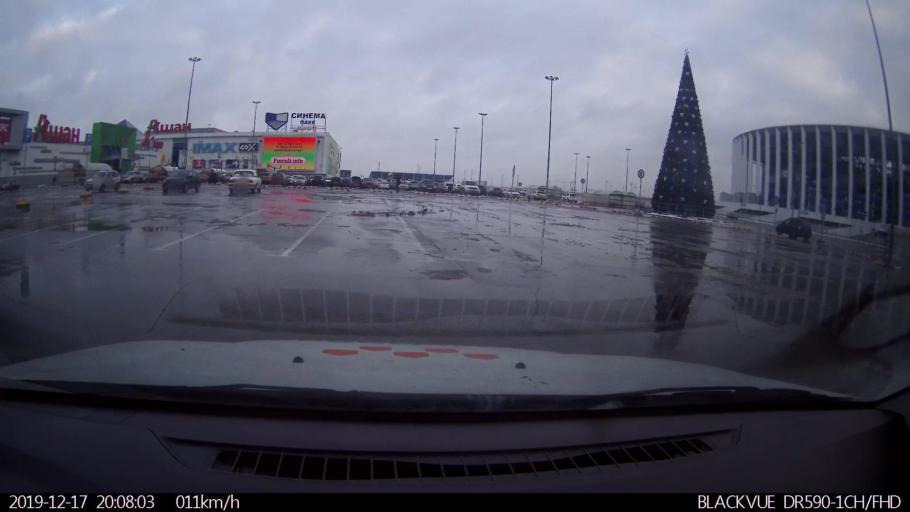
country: RU
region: Nizjnij Novgorod
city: Nizhniy Novgorod
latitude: 56.3378
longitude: 43.9573
